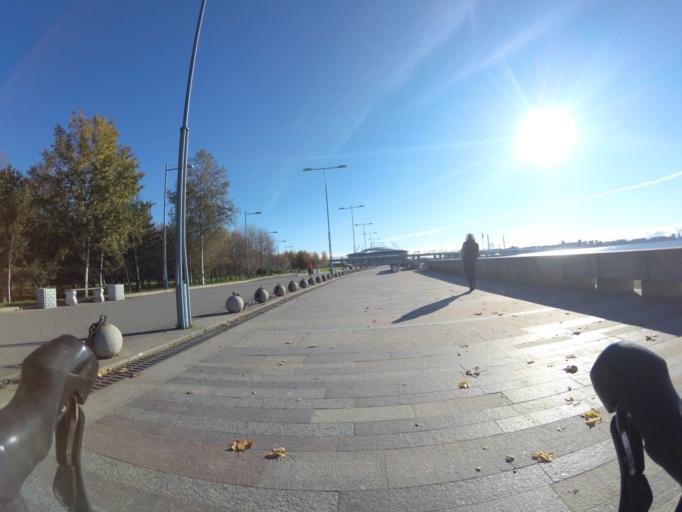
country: RU
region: Leningrad
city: Untolovo
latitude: 59.9810
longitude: 30.2021
